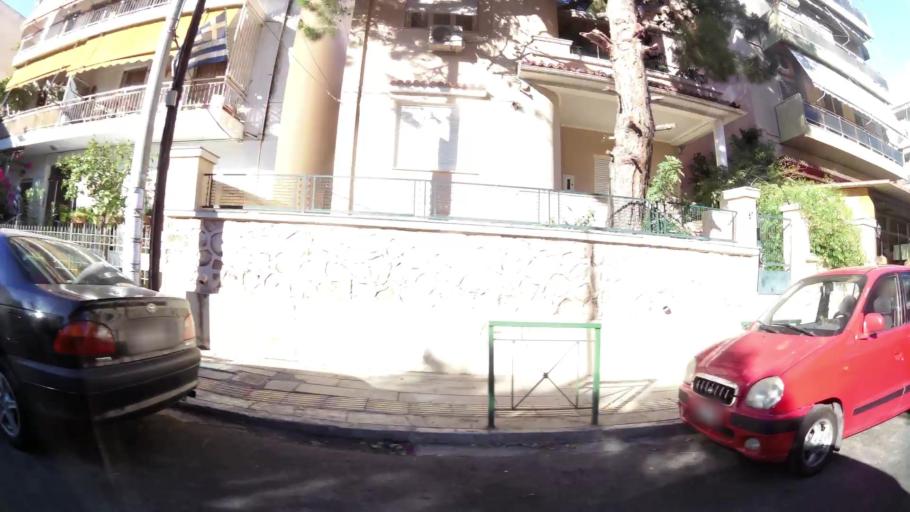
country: GR
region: Attica
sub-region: Nomos Piraios
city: Perama
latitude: 37.9644
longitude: 23.5640
